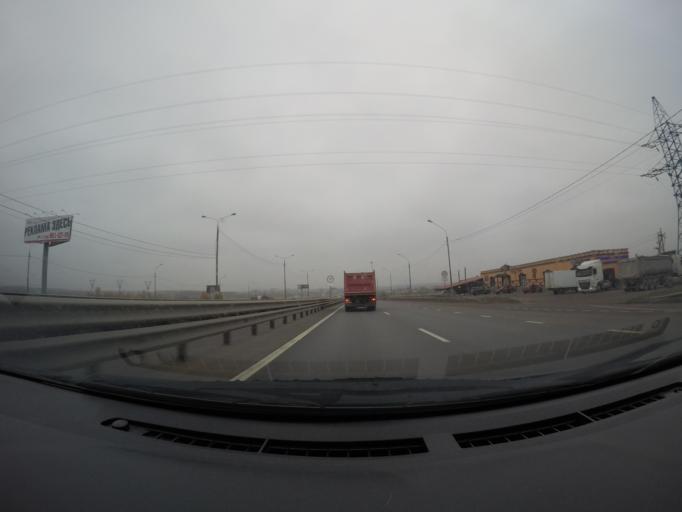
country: RU
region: Moskovskaya
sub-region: Podol'skiy Rayon
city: Podol'sk
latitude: 55.4491
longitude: 37.6185
